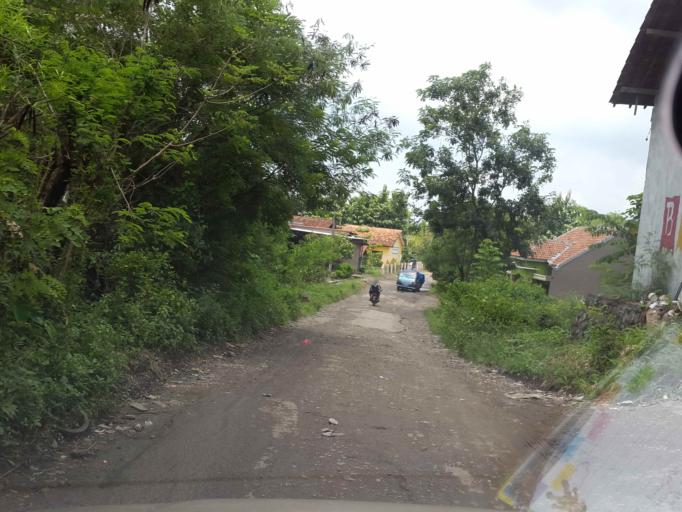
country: ID
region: Central Java
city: Pamedaran
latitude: -7.0170
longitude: 108.9454
